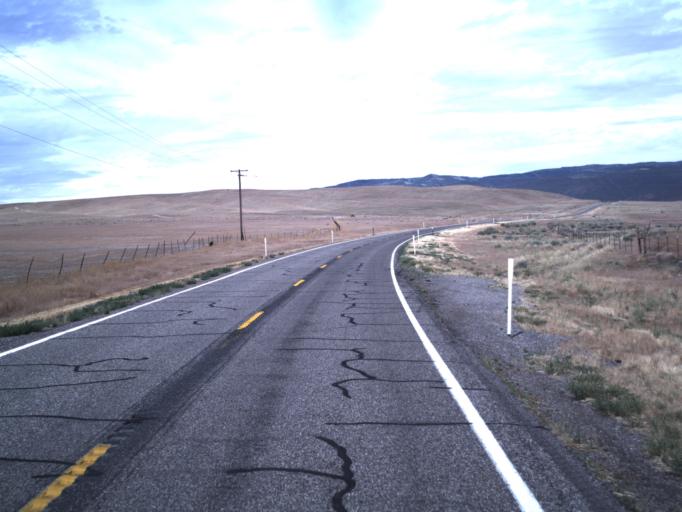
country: US
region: Utah
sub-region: Sevier County
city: Monroe
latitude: 38.6289
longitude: -112.1607
